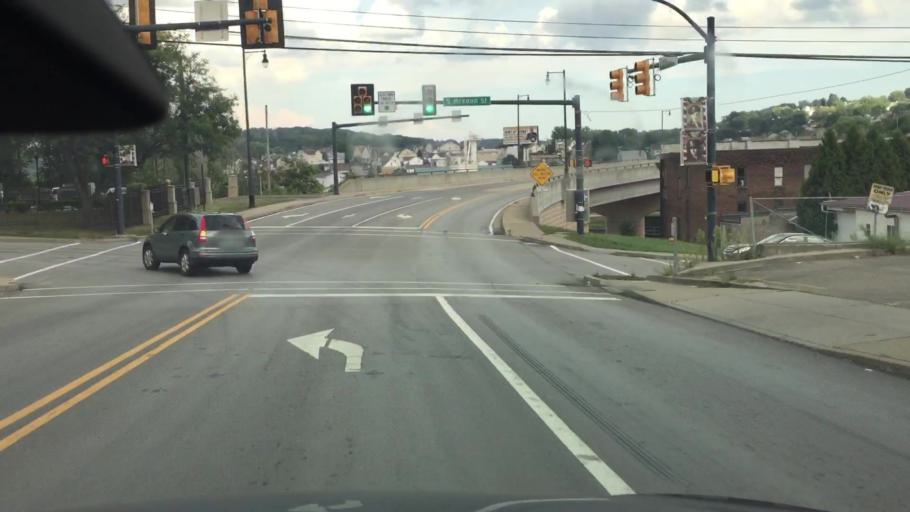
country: US
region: Pennsylvania
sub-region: Butler County
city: Butler
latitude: 40.8558
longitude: -79.8953
